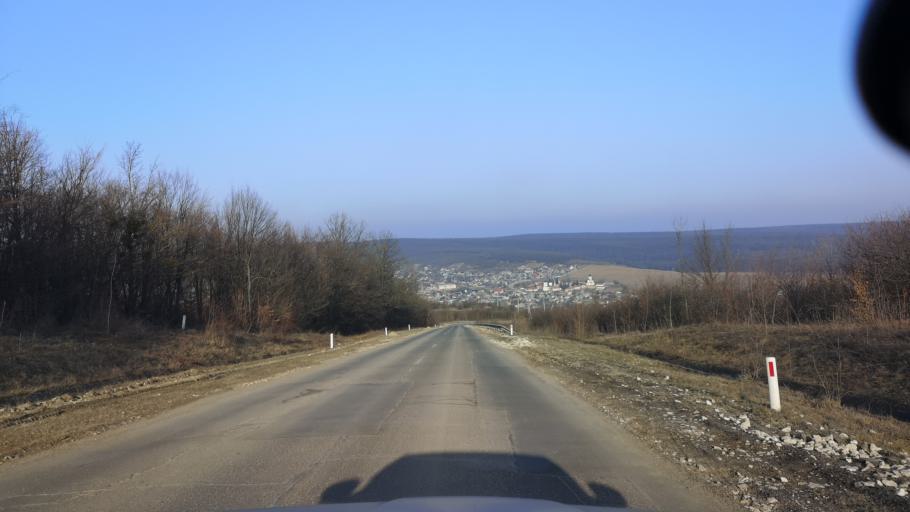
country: MD
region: Stinga Nistrului
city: Bucovat
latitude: 47.1033
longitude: 28.4946
